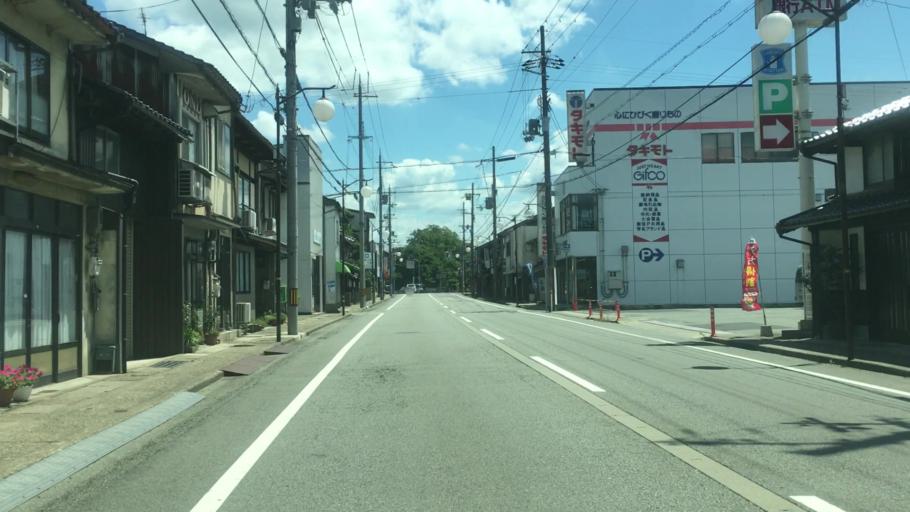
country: JP
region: Hyogo
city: Toyooka
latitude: 35.5368
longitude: 134.8252
